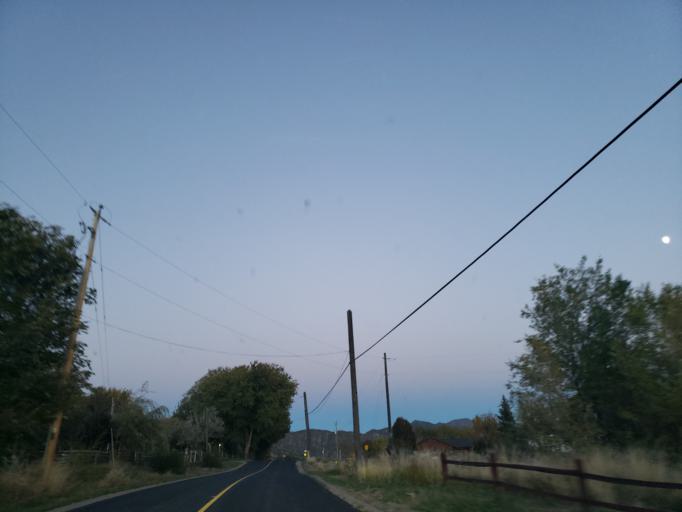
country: US
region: Colorado
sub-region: Garfield County
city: New Castle
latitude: 39.5583
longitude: -107.5828
